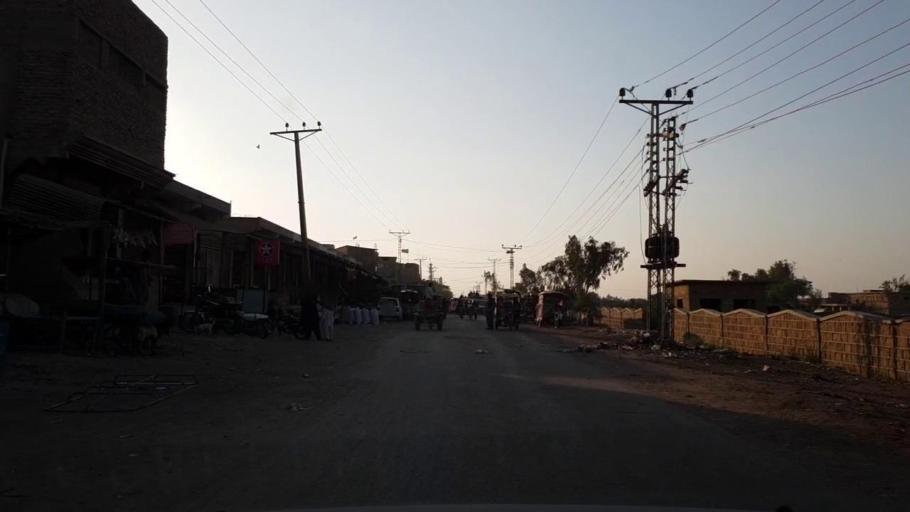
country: PK
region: Sindh
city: Thatta
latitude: 24.6069
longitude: 68.0781
